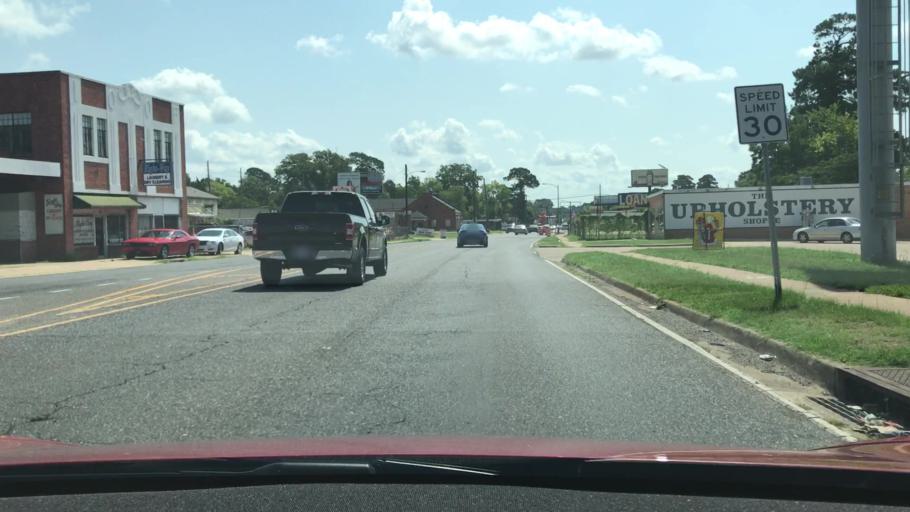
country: US
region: Louisiana
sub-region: Bossier Parish
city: Bossier City
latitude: 32.4419
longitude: -93.7542
